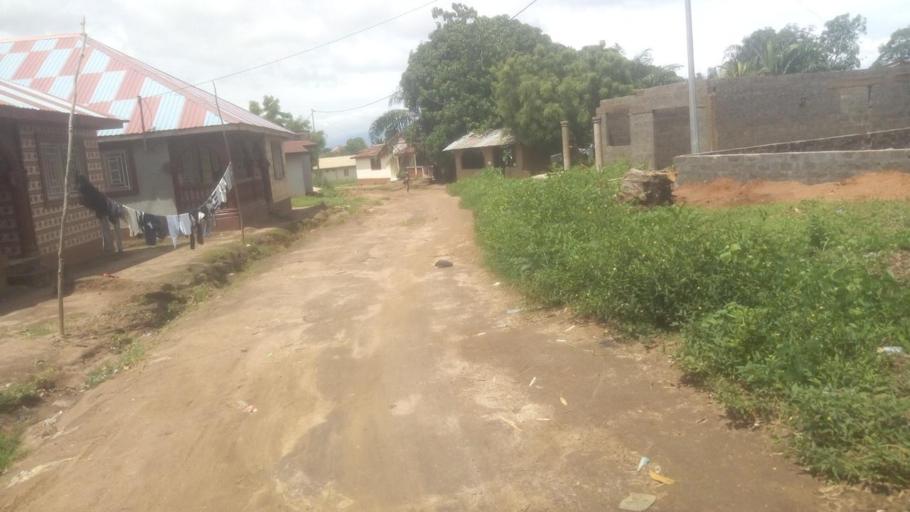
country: SL
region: Northern Province
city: Masoyila
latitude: 8.6006
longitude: -13.1815
